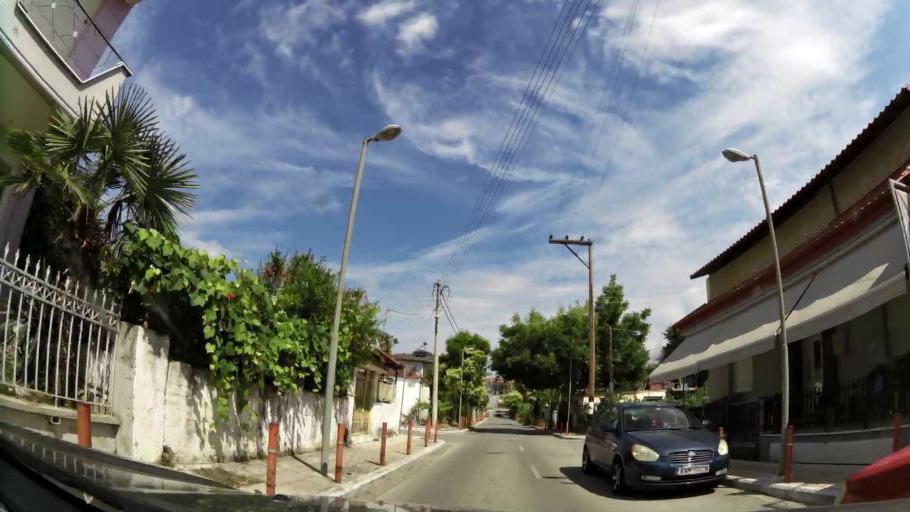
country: GR
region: Central Macedonia
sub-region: Nomos Pierias
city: Katerini
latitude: 40.2625
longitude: 22.4968
